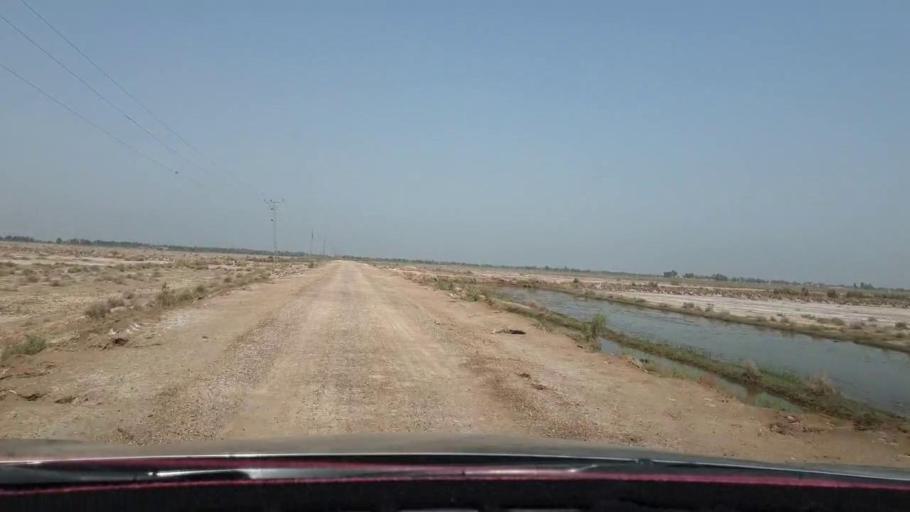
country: PK
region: Sindh
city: Warah
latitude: 27.3885
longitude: 67.6817
